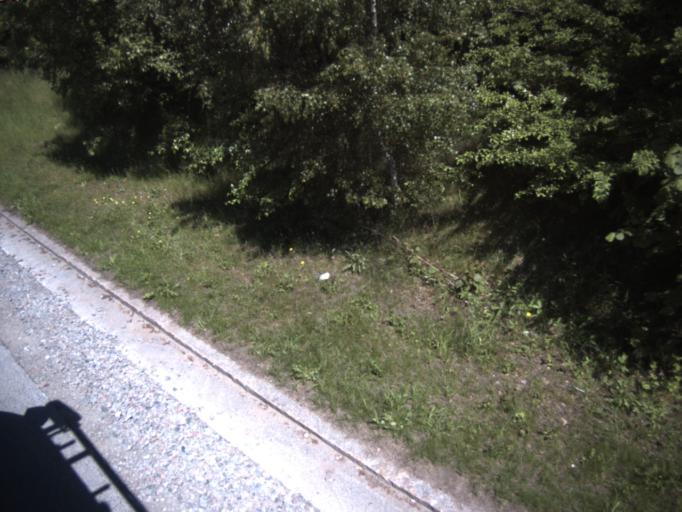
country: SE
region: Skane
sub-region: Helsingborg
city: Gantofta
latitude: 56.0052
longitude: 12.7765
